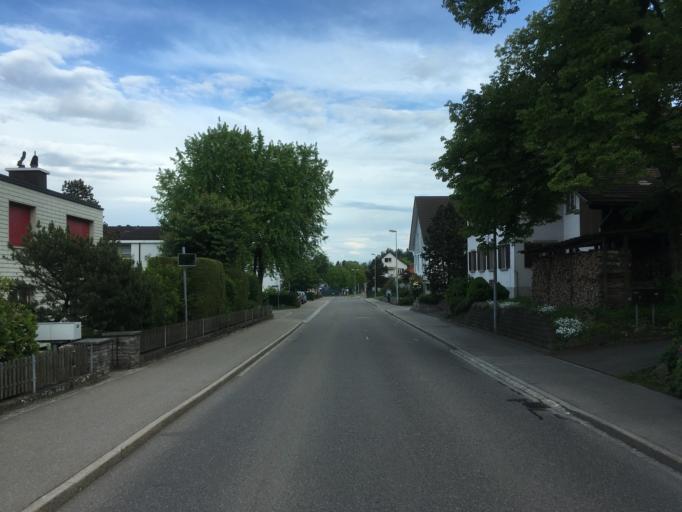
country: CH
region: Zurich
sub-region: Bezirk Uster
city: Binz
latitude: 47.3580
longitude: 8.6266
